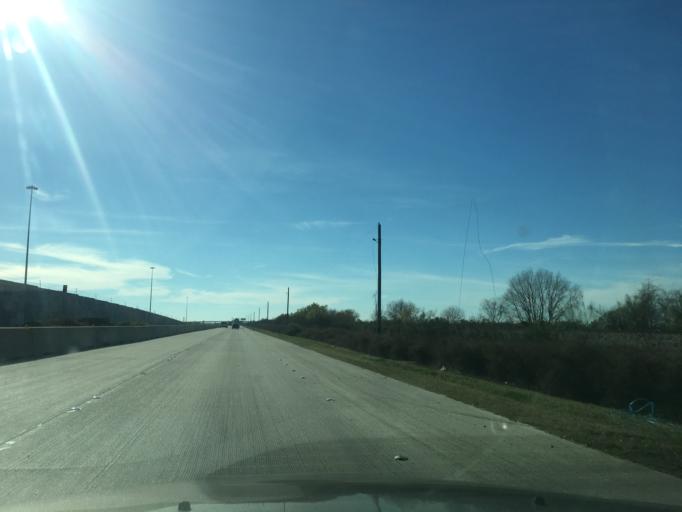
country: US
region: Texas
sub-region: Fort Bend County
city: Rosenberg
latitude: 29.5330
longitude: -95.8604
